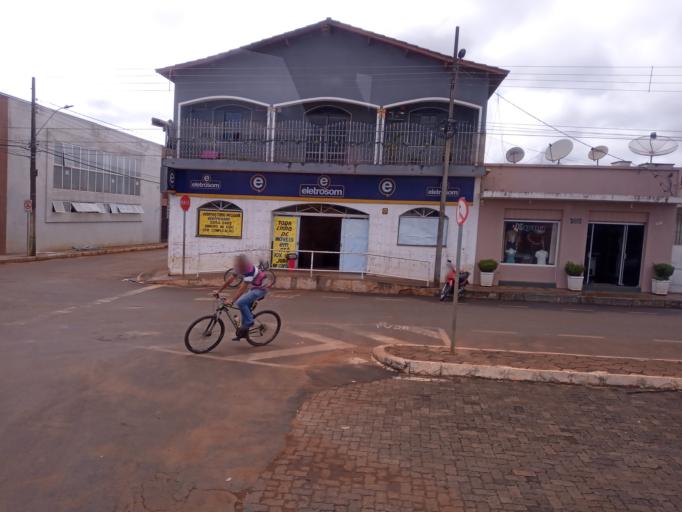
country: BR
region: Minas Gerais
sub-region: Sacramento
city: Sacramento
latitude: -19.3126
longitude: -47.5271
